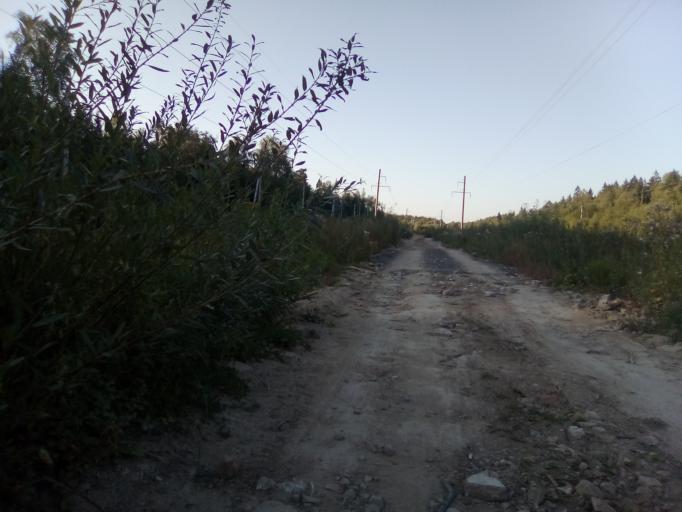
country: RU
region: Moskovskaya
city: Aprelevka
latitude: 55.5737
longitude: 37.0657
